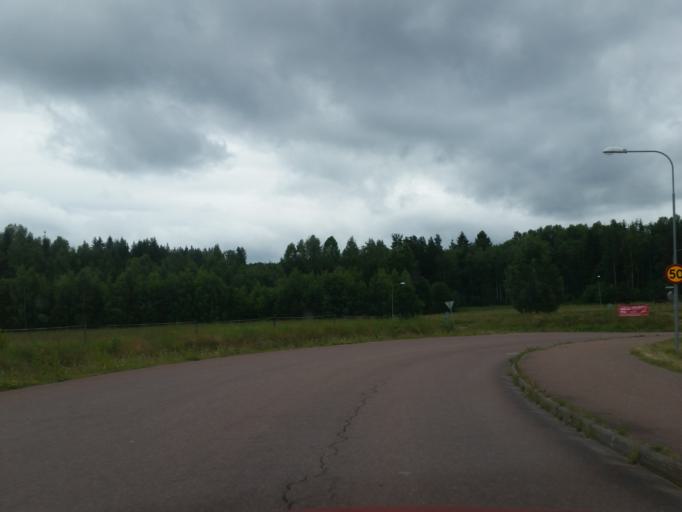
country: SE
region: Dalarna
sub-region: Leksand Municipality
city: Smedby
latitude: 60.6694
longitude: 15.1026
